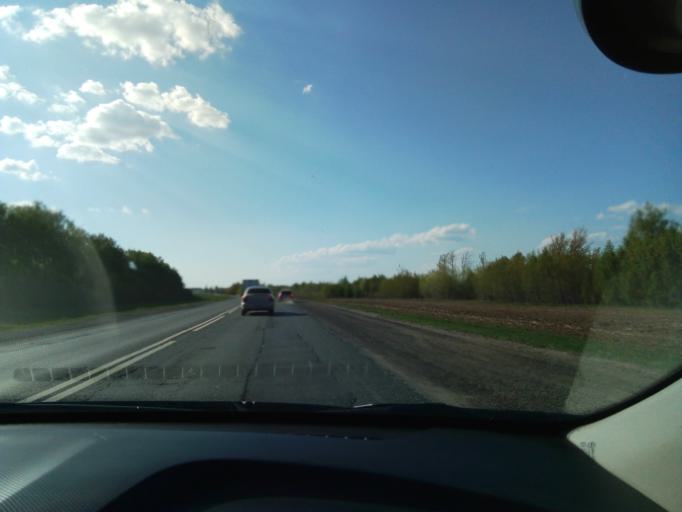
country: RU
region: Chuvashia
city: Kugesi
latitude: 56.0527
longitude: 47.2784
